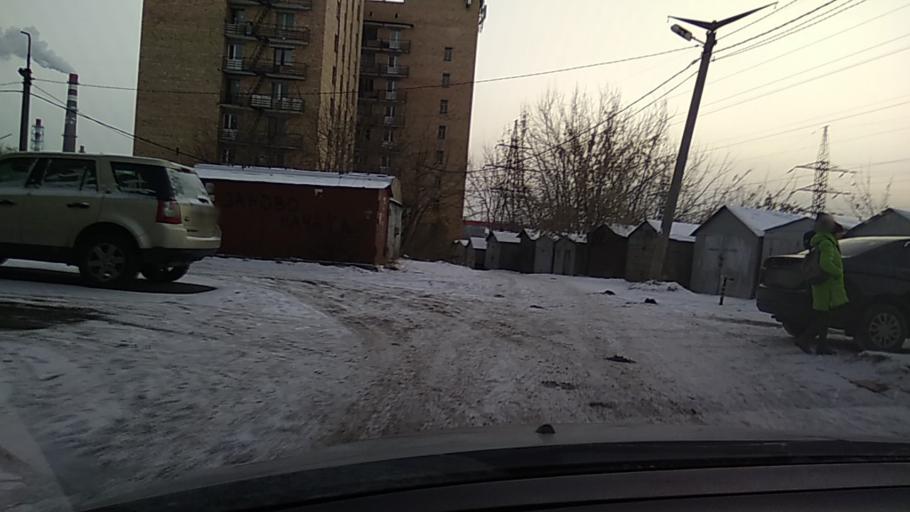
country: RU
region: Sverdlovsk
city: Istok
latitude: 56.7617
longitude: 60.7142
